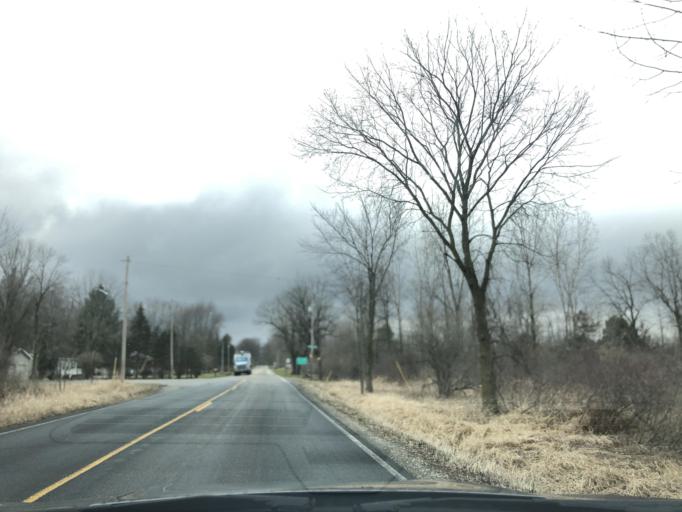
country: US
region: Michigan
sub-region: Clinton County
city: Fowler
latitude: 43.1046
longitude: -84.6791
